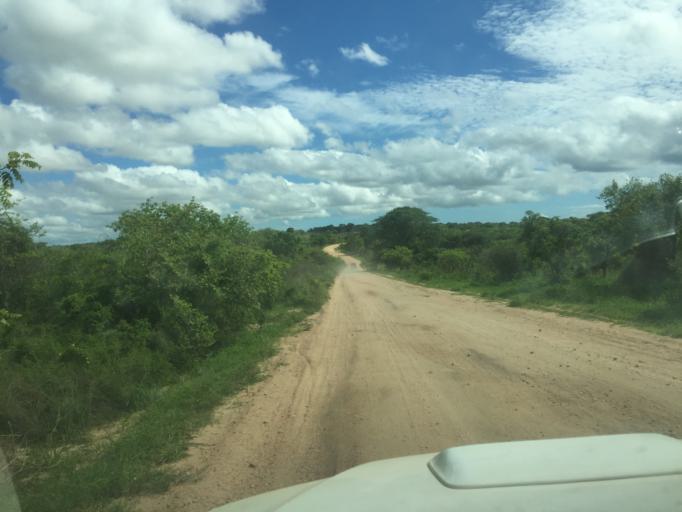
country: MZ
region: Nampula
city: Nacala
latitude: -14.2282
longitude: 40.5095
